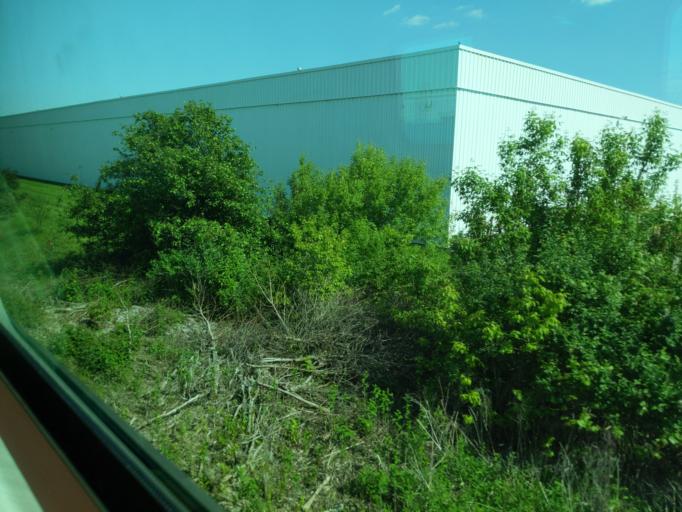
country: CA
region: Ontario
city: Etobicoke
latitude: 43.7049
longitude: -79.6292
